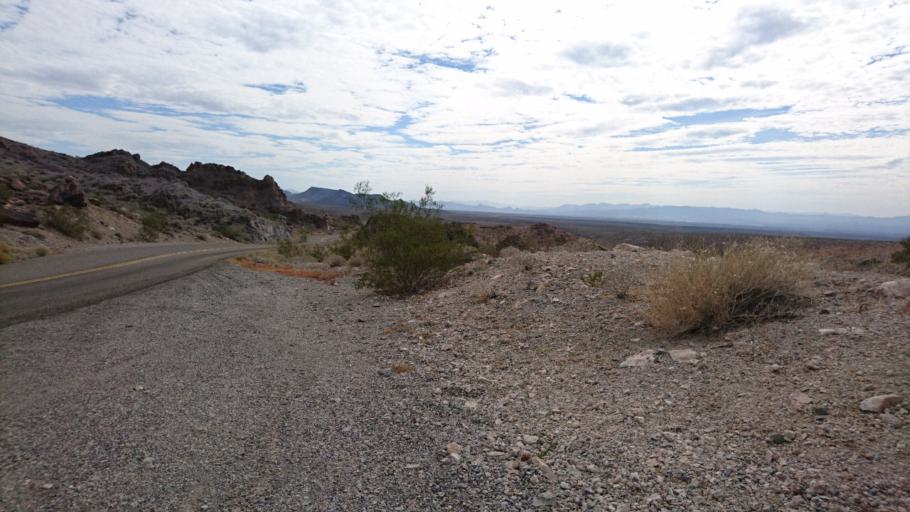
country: US
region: Arizona
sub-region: Mohave County
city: Mohave Valley
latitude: 34.9830
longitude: -114.4244
